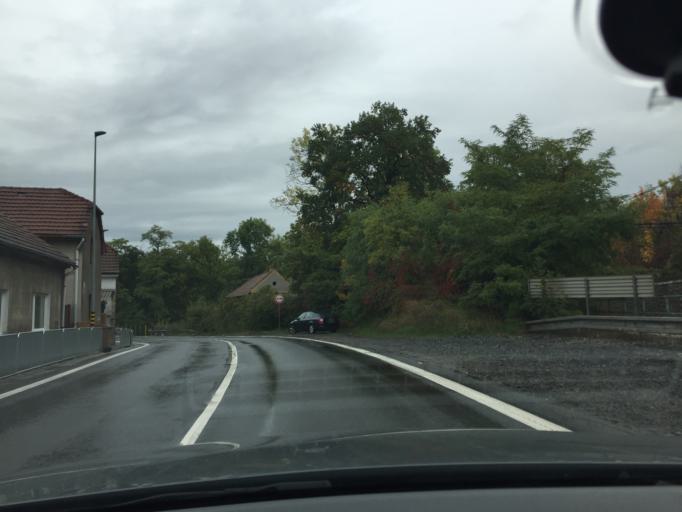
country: CZ
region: Central Bohemia
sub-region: Okres Melnik
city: Veltrusy
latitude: 50.3038
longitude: 14.3174
